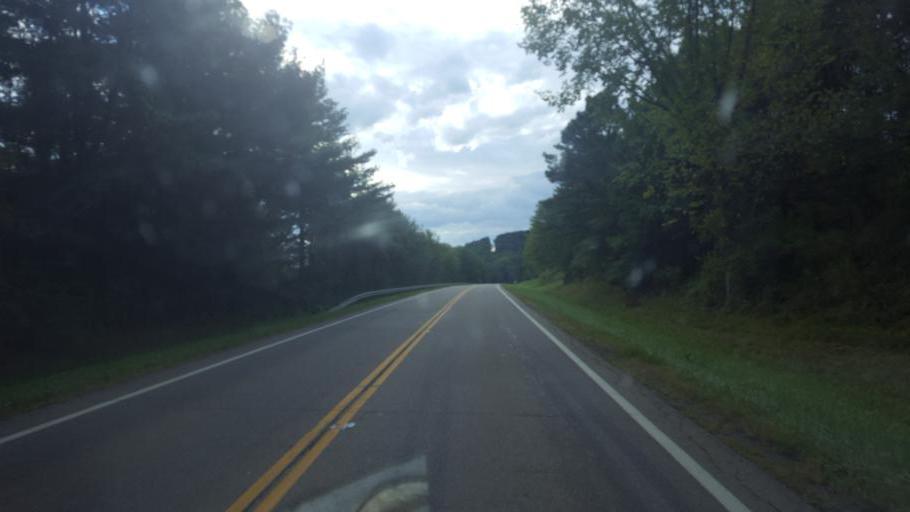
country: US
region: Ohio
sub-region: Holmes County
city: Millersburg
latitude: 40.4815
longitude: -82.0167
